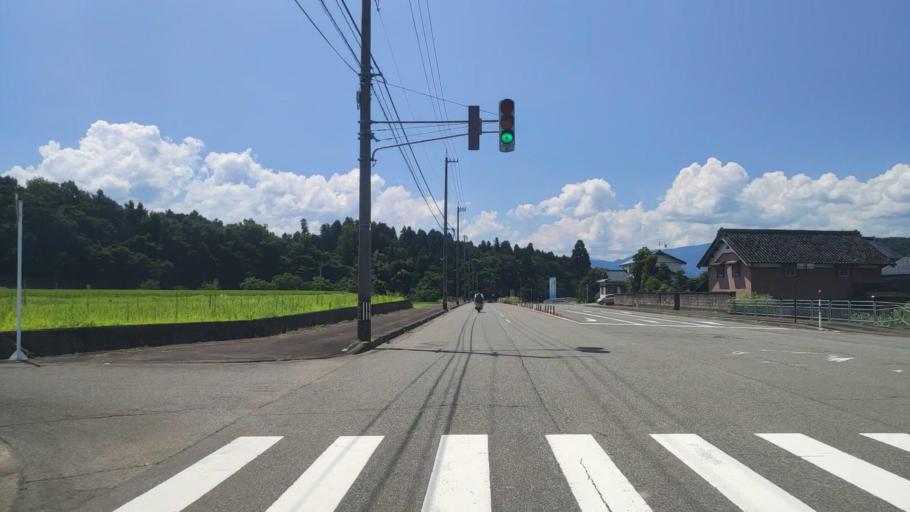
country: JP
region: Fukui
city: Katsuyama
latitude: 36.0337
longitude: 136.5202
